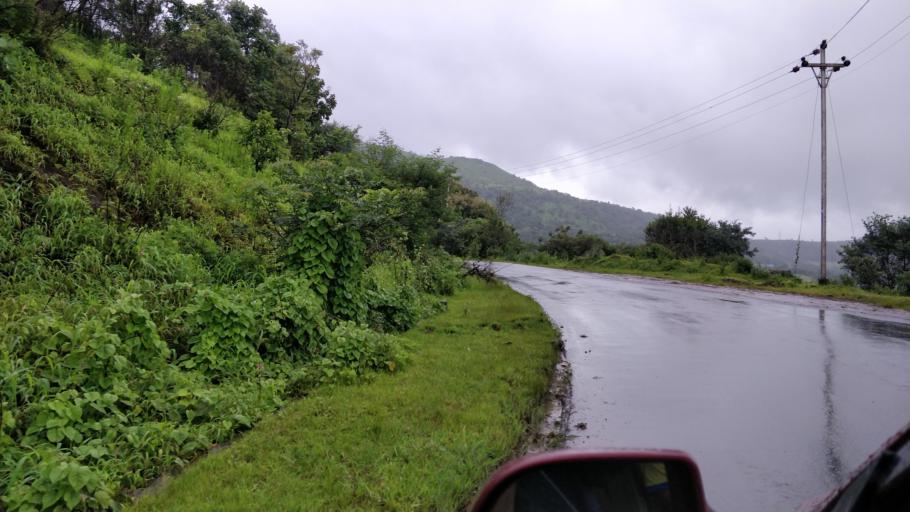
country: IN
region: Maharashtra
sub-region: Pune Division
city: Kharakvasla
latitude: 18.4762
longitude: 73.6535
